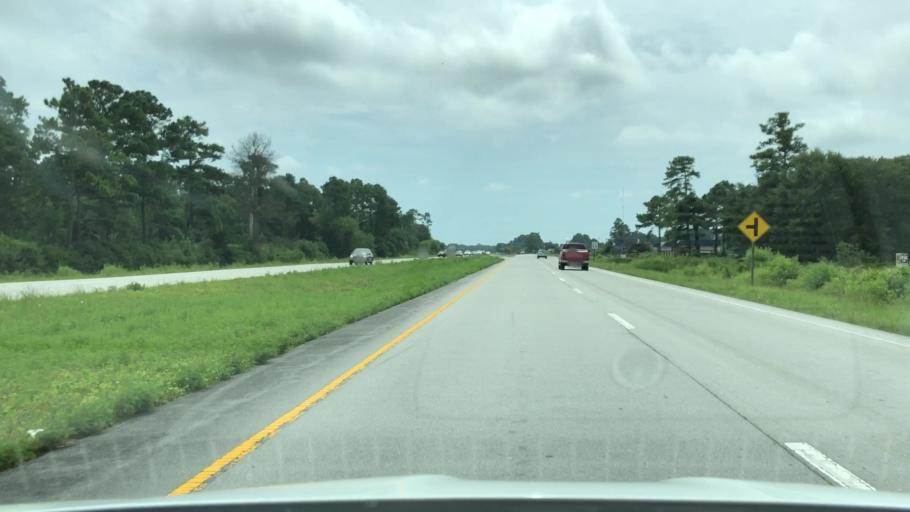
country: US
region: North Carolina
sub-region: Carteret County
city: Newport
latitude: 34.7956
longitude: -76.8777
